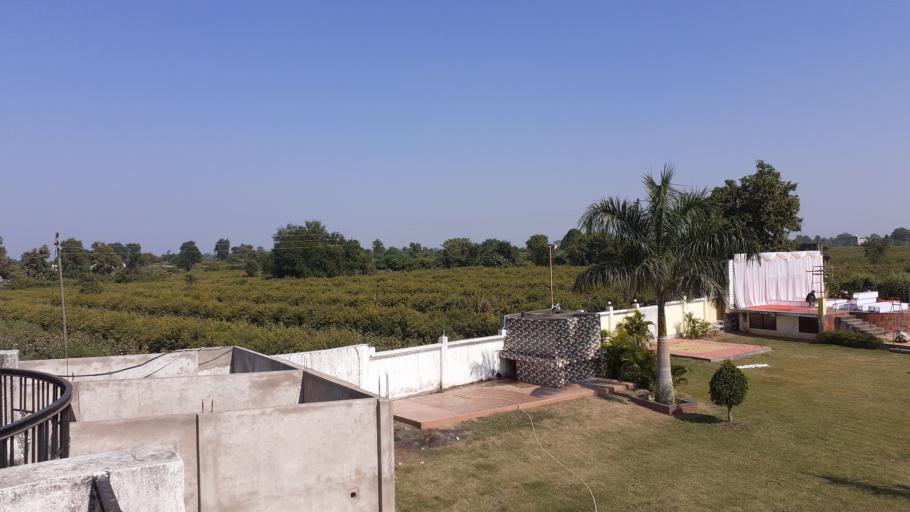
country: IN
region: Maharashtra
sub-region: Nagpur Division
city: Koradih
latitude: 21.3010
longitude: 79.0755
